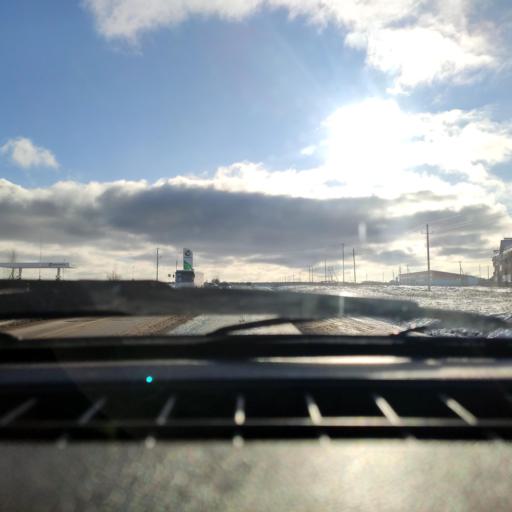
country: RU
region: Bashkortostan
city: Iglino
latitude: 54.8026
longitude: 56.4129
